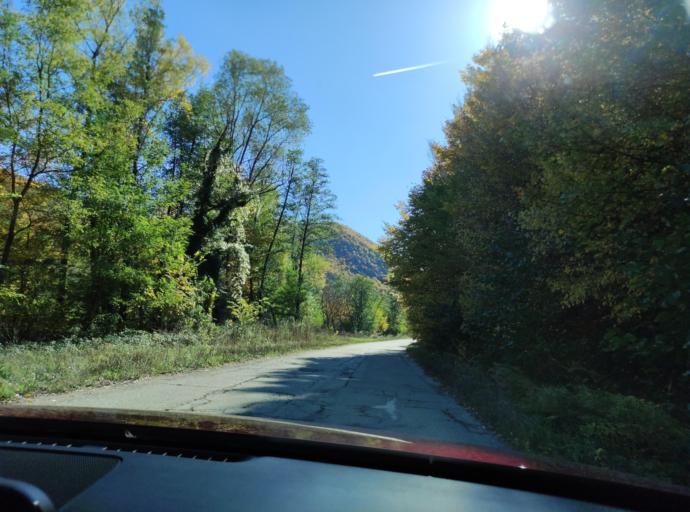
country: BG
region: Montana
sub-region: Obshtina Chiprovtsi
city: Chiprovtsi
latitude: 43.4098
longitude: 22.9388
